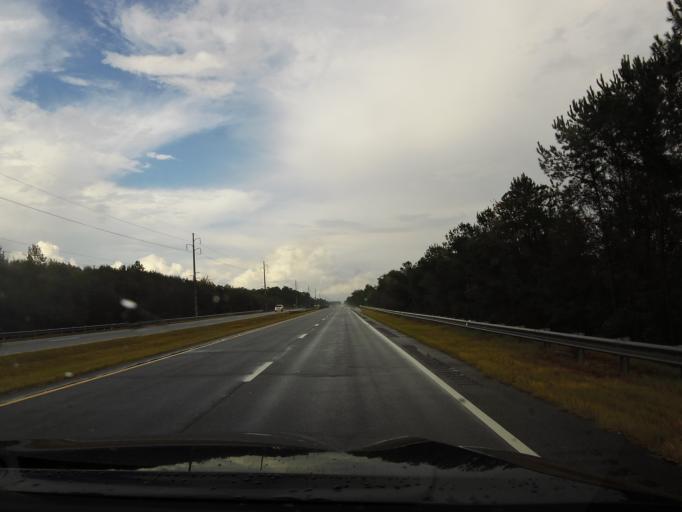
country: US
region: Georgia
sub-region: Long County
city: Ludowici
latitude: 31.6935
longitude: -81.7826
